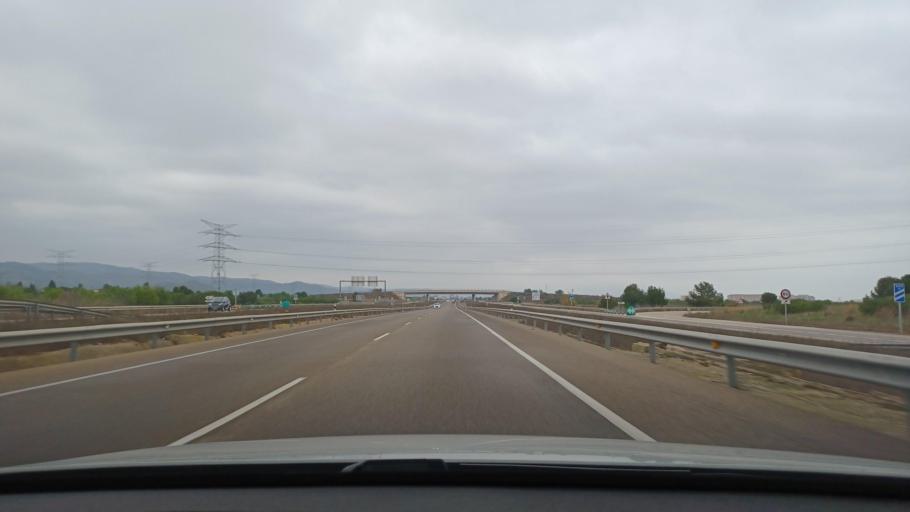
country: ES
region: Valencia
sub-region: Provincia de Castello
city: Orpesa/Oropesa del Mar
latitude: 40.1225
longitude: 0.1436
